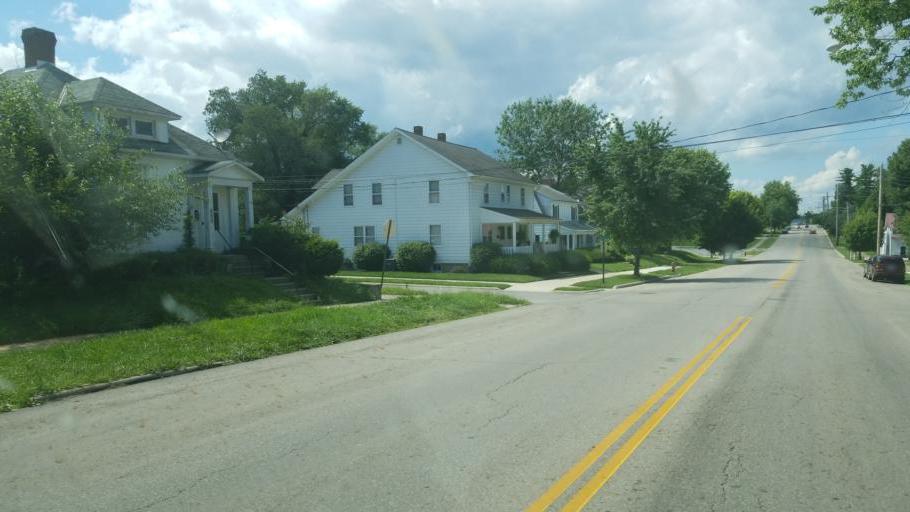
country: US
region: Ohio
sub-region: Highland County
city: Greenfield
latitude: 39.3554
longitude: -83.3843
